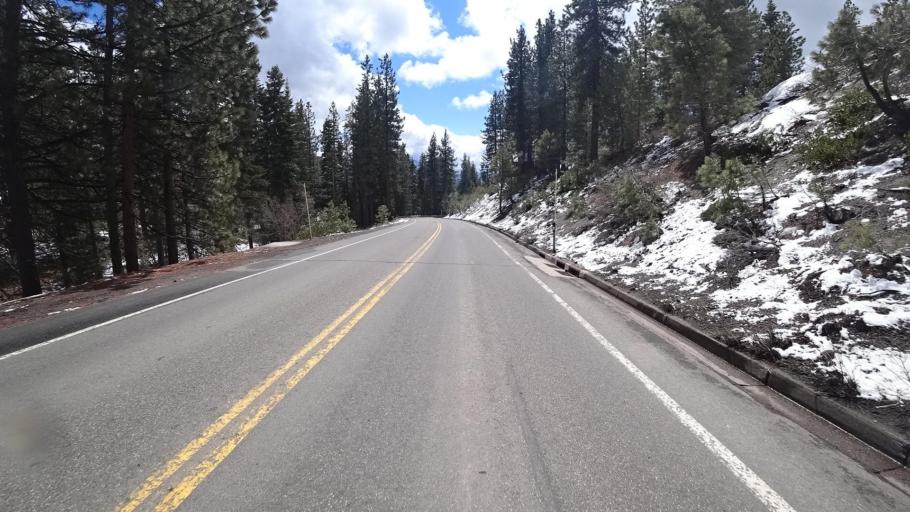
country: US
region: Nevada
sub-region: Washoe County
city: Incline Village
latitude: 39.2719
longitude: -119.9467
